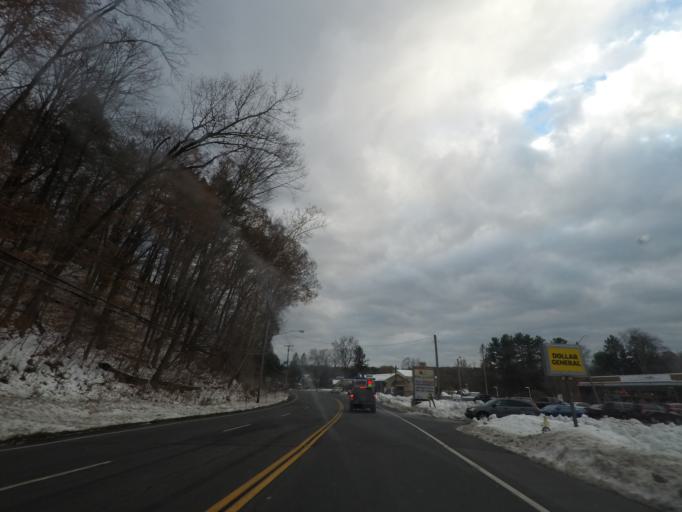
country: US
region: New York
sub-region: Ulster County
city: Rosendale Village
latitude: 41.8496
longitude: -74.0752
